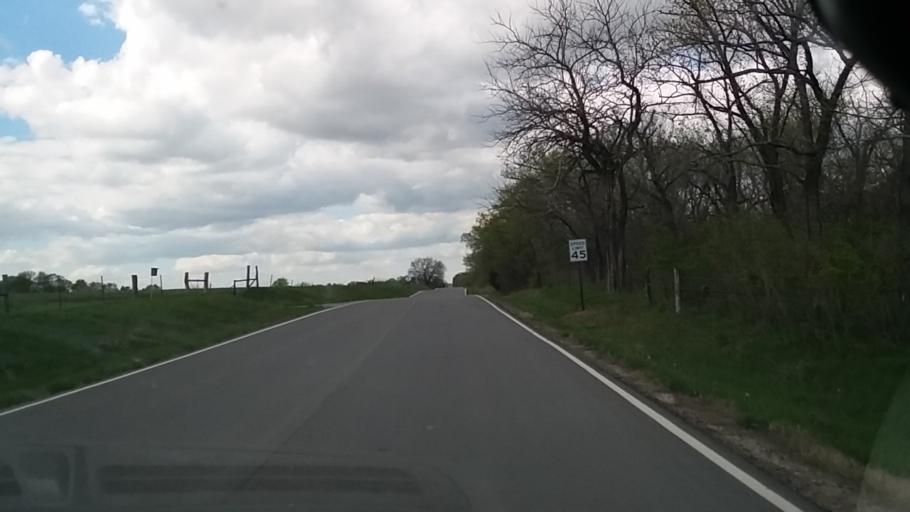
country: US
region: Kansas
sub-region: Douglas County
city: Lawrence
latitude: 38.8851
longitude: -95.2418
